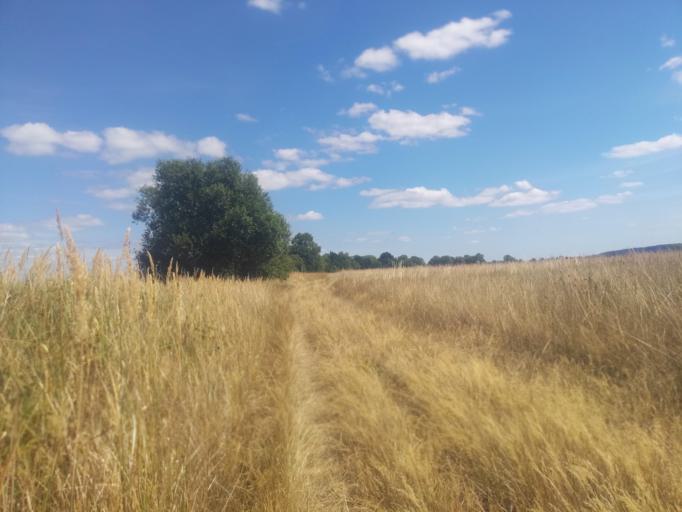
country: DE
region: Lower Saxony
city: Tosterglope
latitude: 53.2548
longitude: 10.8319
